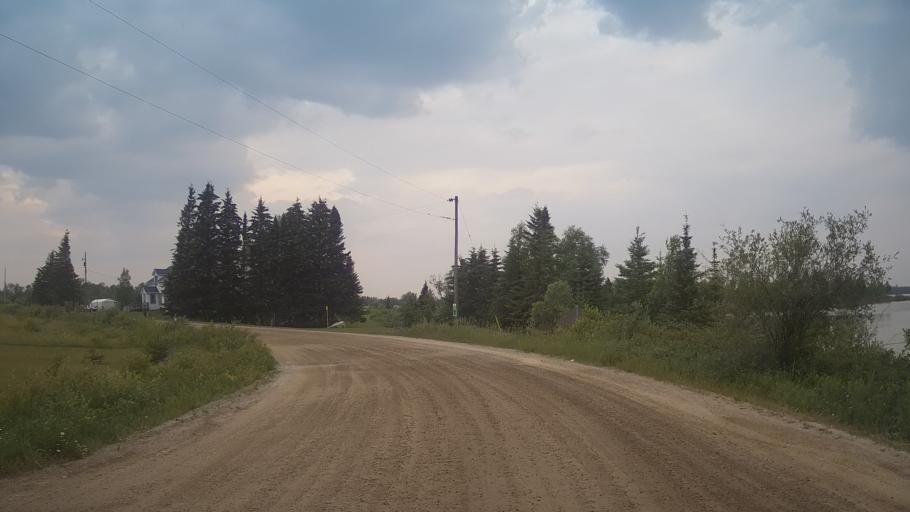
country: CA
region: Ontario
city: Hearst
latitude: 49.6441
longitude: -83.2789
